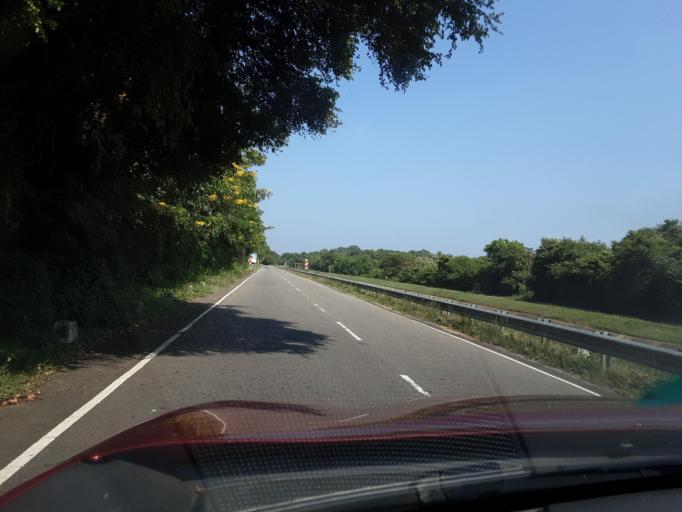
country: LK
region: Uva
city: Badulla
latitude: 7.2782
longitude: 81.0445
